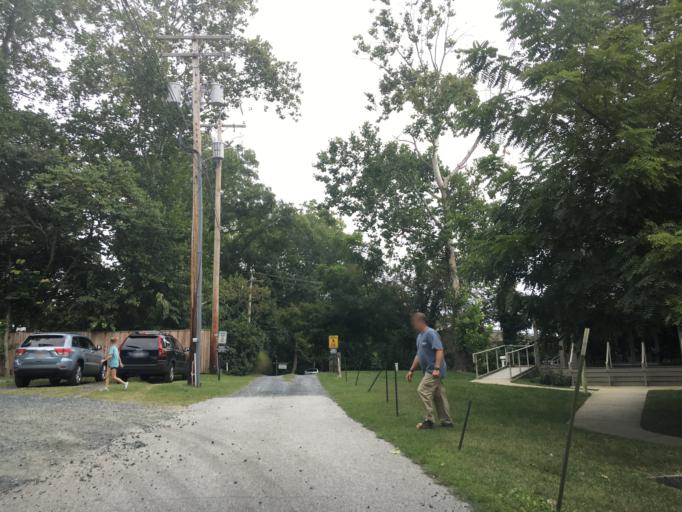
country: US
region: Maryland
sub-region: Anne Arundel County
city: Herald Harbor
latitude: 39.0428
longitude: -76.5760
